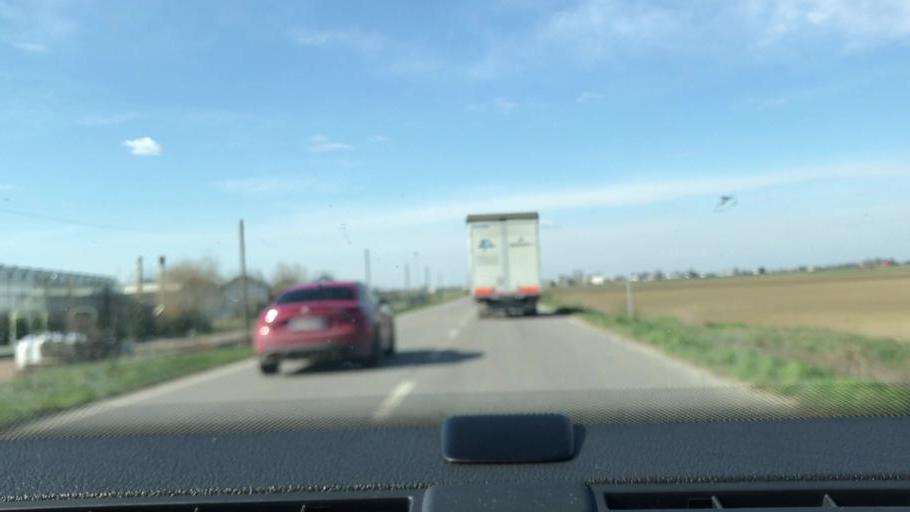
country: IT
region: Veneto
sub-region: Provincia di Rovigo
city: Calto
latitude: 45.0030
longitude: 11.3498
